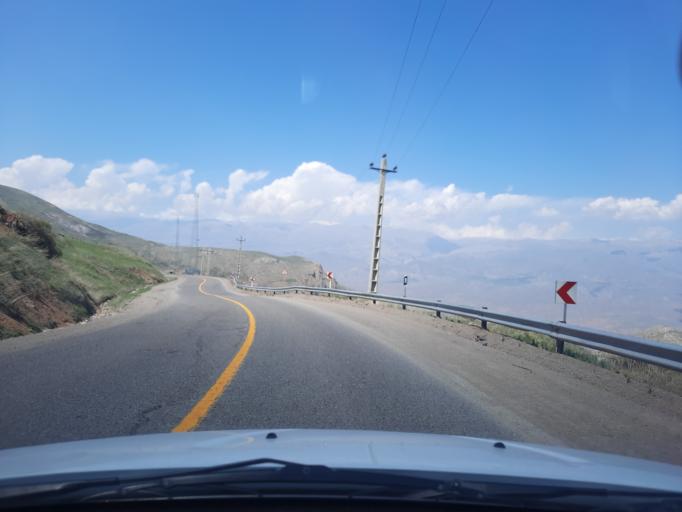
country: IR
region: Qazvin
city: Qazvin
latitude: 36.4039
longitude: 50.2224
